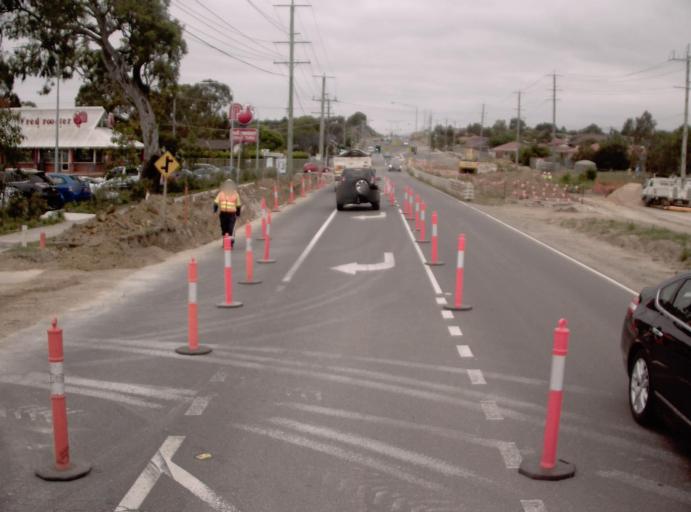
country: AU
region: Victoria
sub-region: Casey
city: Hallam
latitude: -38.0332
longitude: 145.2676
